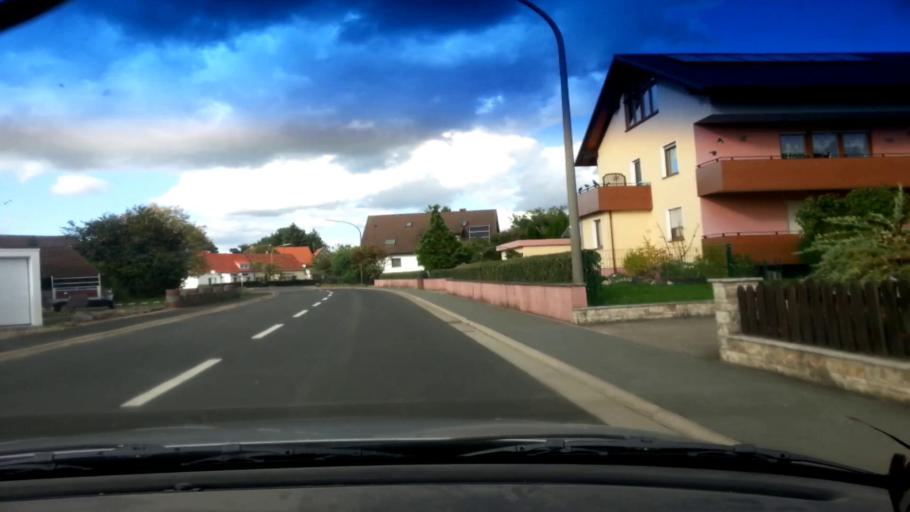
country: DE
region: Bavaria
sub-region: Upper Franconia
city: Ebensfeld
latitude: 50.0662
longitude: 10.9526
